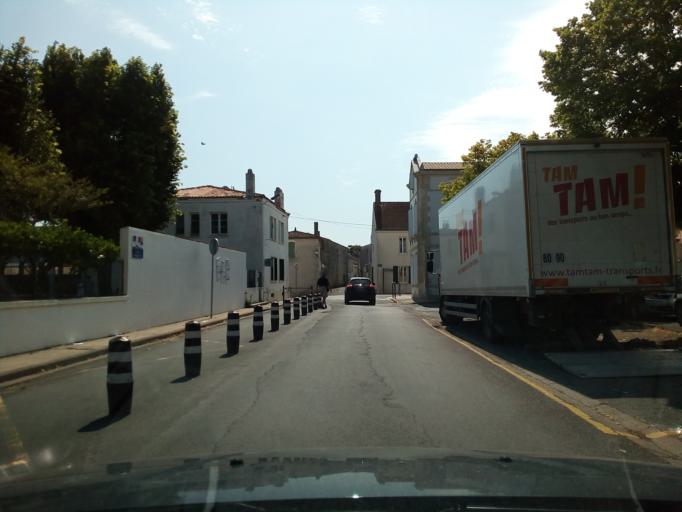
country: FR
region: Poitou-Charentes
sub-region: Departement de la Charente-Maritime
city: Dolus-d'Oleron
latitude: 45.9455
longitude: -1.3057
